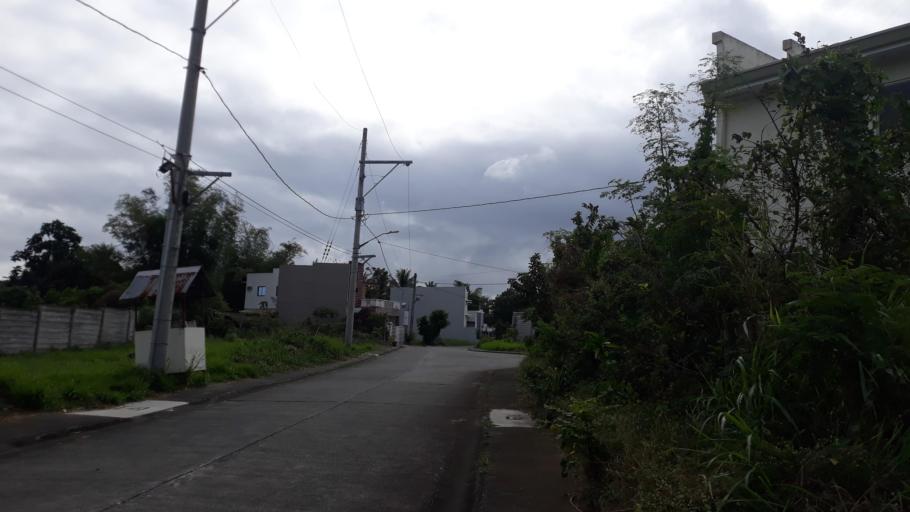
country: PH
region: Calabarzon
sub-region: Province of Cavite
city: Biga
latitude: 14.2752
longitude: 120.9707
